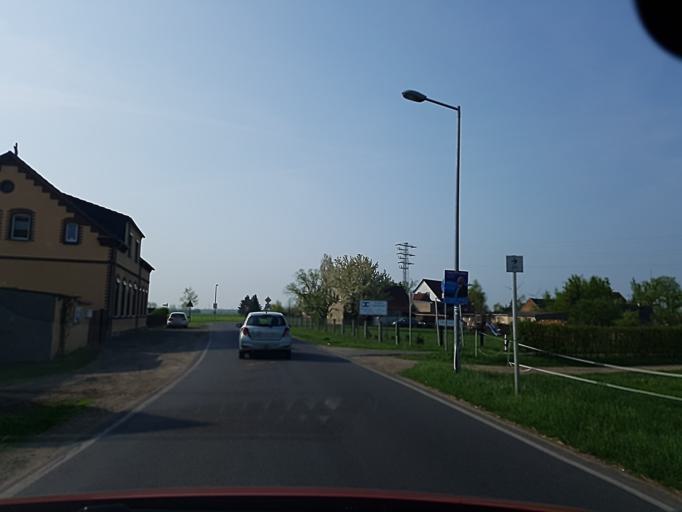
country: DE
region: Brandenburg
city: Falkenberg
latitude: 51.5851
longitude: 13.2135
